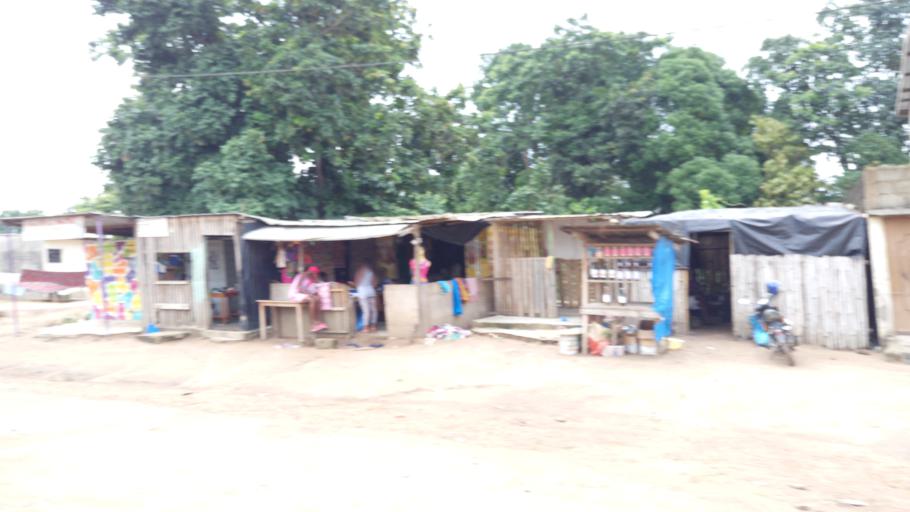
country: CI
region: Lagunes
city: Abobo
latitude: 5.4111
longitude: -3.9960
